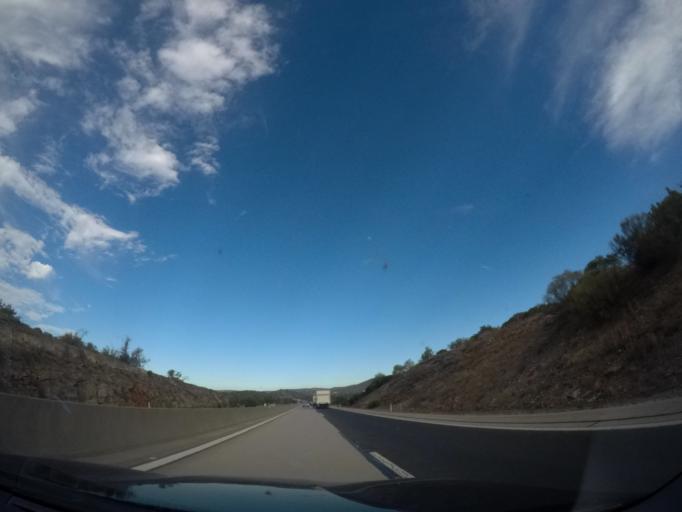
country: PT
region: Faro
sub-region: Loule
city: Vilamoura
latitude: 37.1257
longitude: -8.0877
